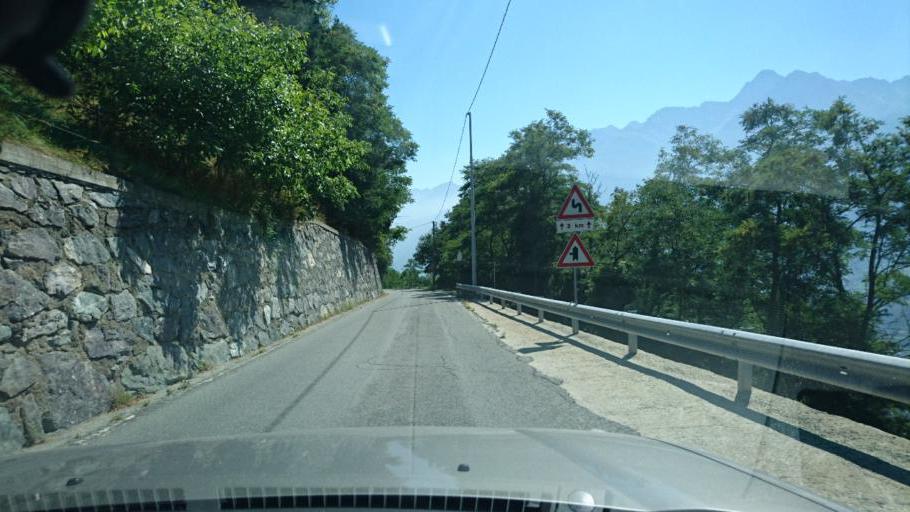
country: IT
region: Aosta Valley
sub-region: Valle d'Aosta
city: Montan-Angelin-Arensod
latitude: 45.7484
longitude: 7.2868
